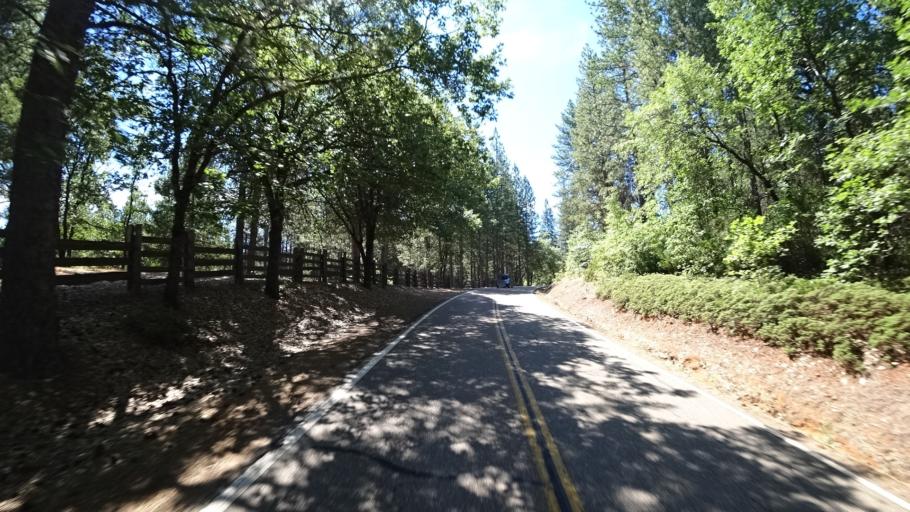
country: US
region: California
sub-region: Amador County
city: Pioneer
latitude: 38.3383
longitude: -120.5684
